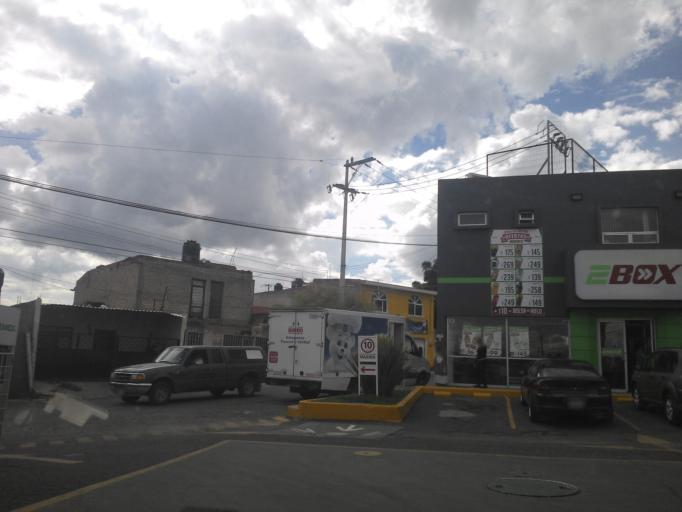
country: MX
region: Jalisco
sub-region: Tlajomulco de Zuniga
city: Palomar
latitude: 20.6532
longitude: -103.4525
